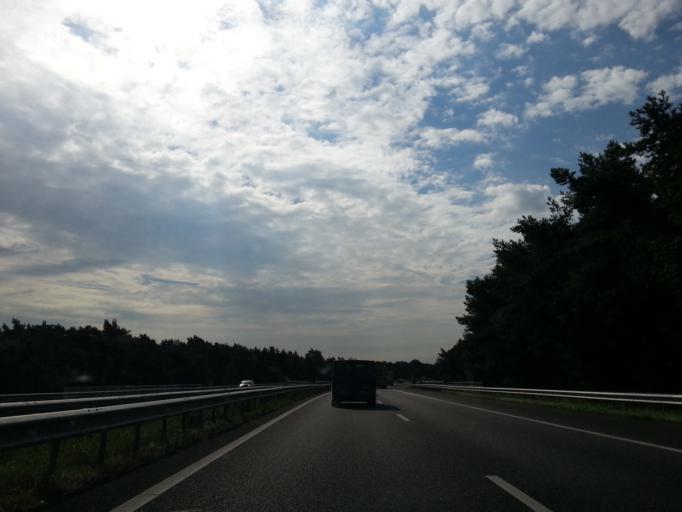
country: NL
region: North Brabant
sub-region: Gemeente Cranendonck
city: Cranendonck
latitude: 51.2909
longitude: 5.6412
